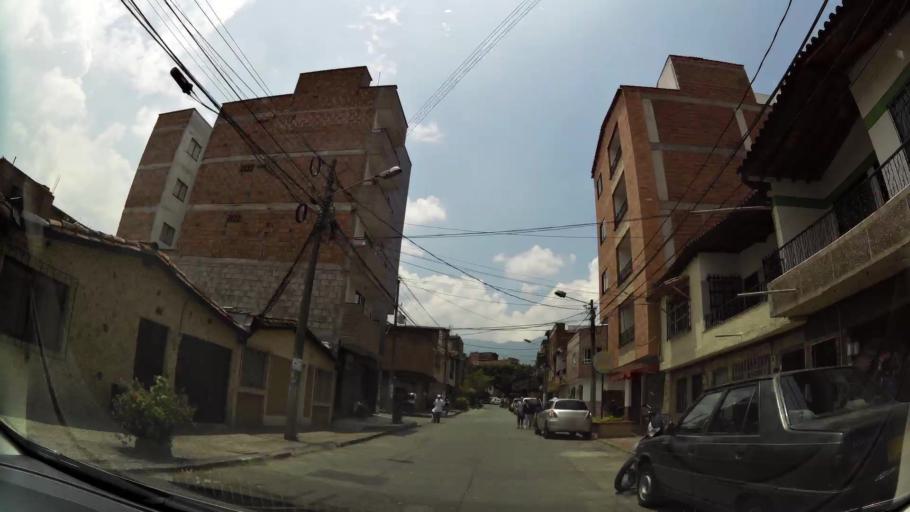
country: CO
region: Antioquia
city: Sabaneta
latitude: 6.1680
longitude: -75.6139
